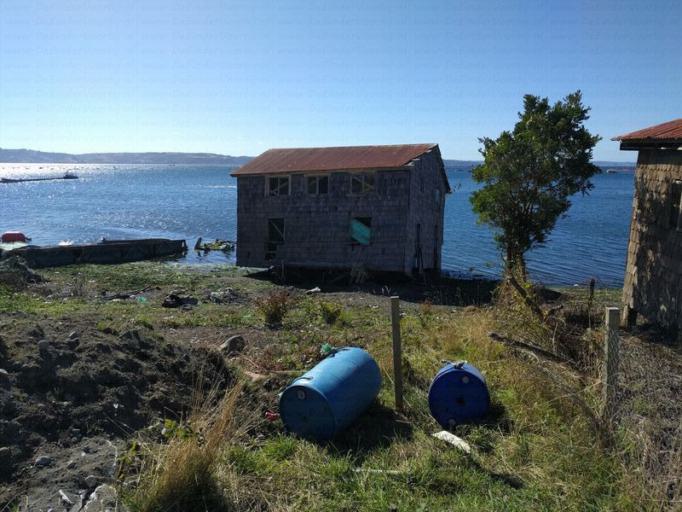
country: CL
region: Los Lagos
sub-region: Provincia de Chiloe
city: Castro
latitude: -42.3958
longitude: -73.5609
